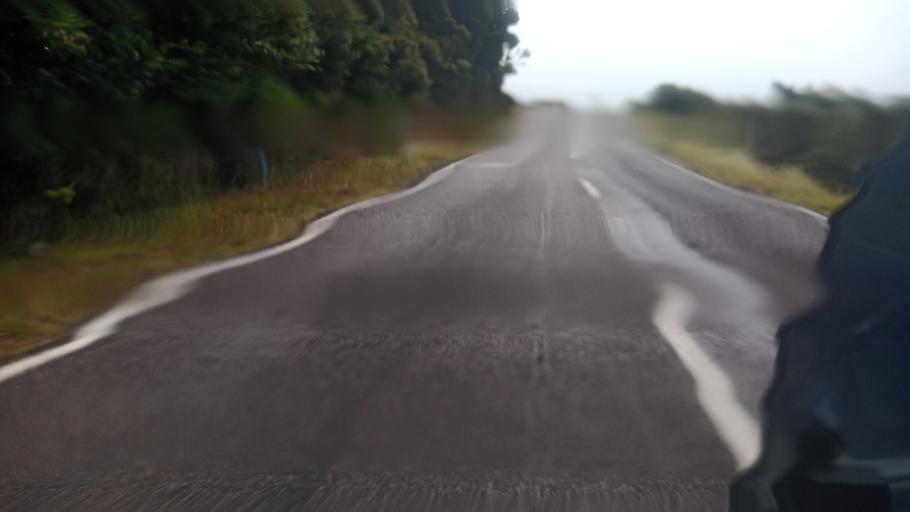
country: NZ
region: Bay of Plenty
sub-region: Opotiki District
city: Opotiki
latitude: -37.6599
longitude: 177.8212
